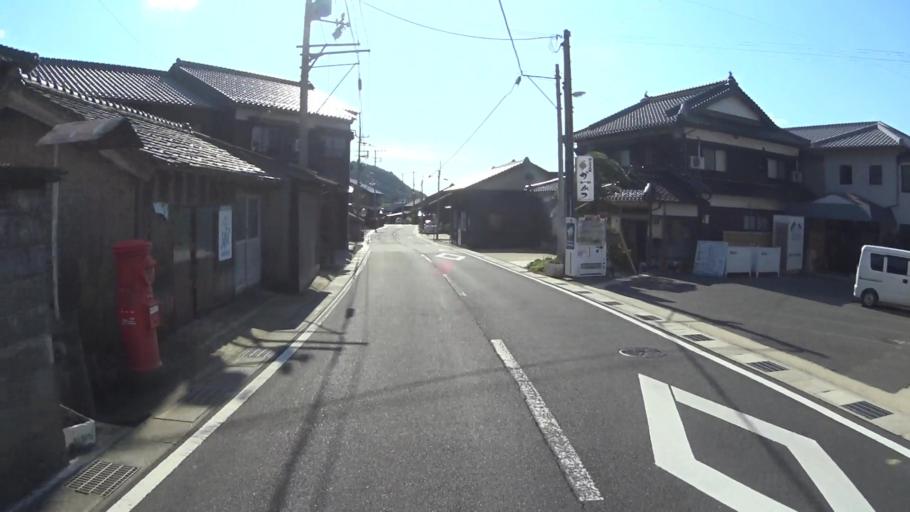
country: JP
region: Kyoto
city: Miyazu
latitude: 35.7209
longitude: 135.0811
